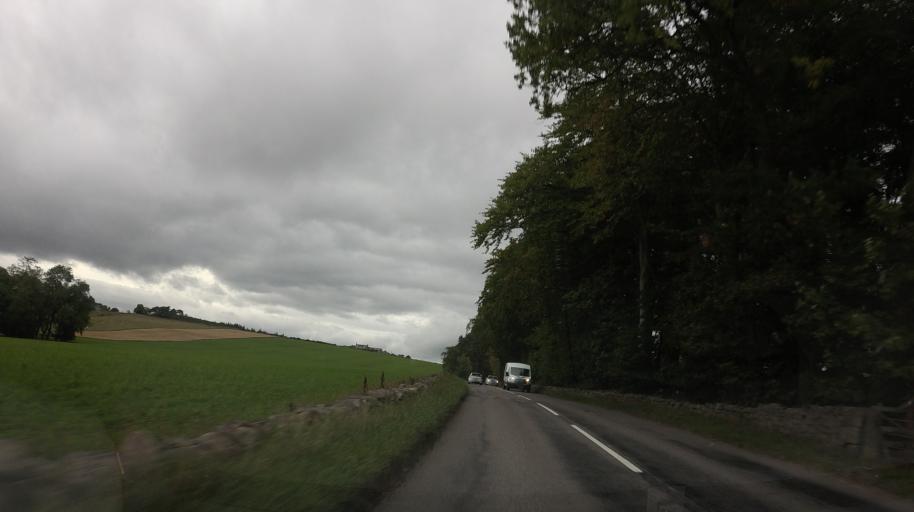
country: GB
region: Scotland
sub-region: Aberdeenshire
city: Kemnay
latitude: 57.1582
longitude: -2.4312
